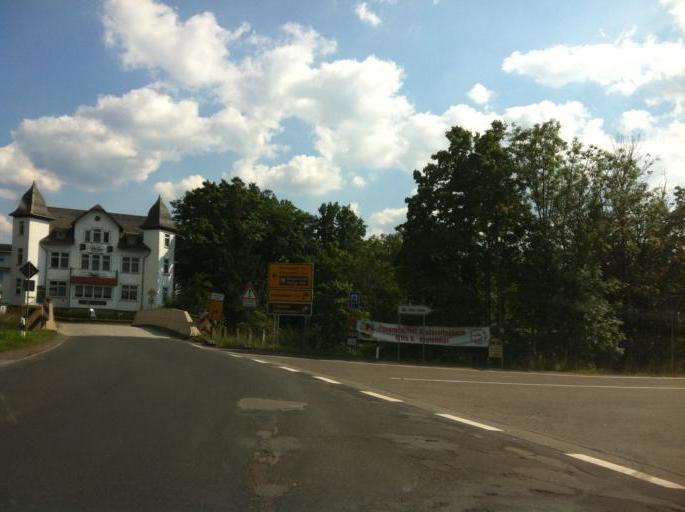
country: DE
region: Thuringia
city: Grossbreitenbach
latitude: 50.5945
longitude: 10.9842
